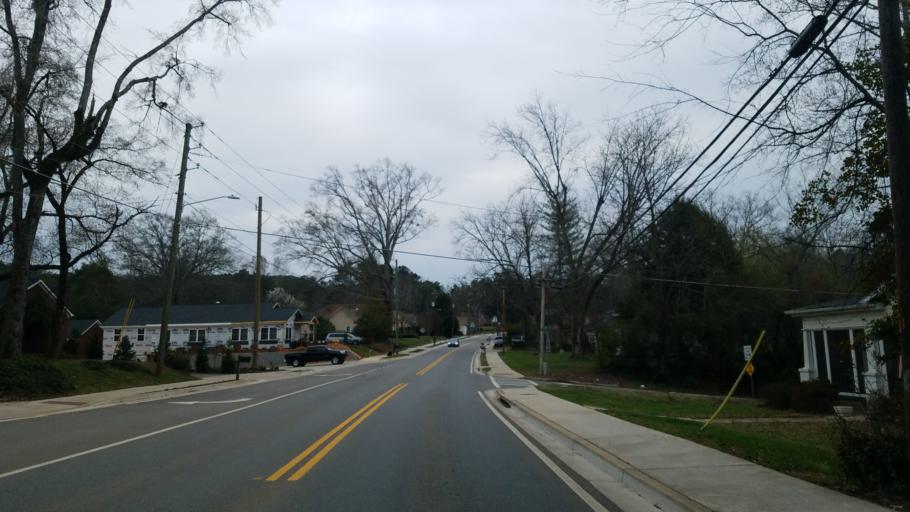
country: US
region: Georgia
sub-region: Cherokee County
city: Canton
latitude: 34.2243
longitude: -84.4941
